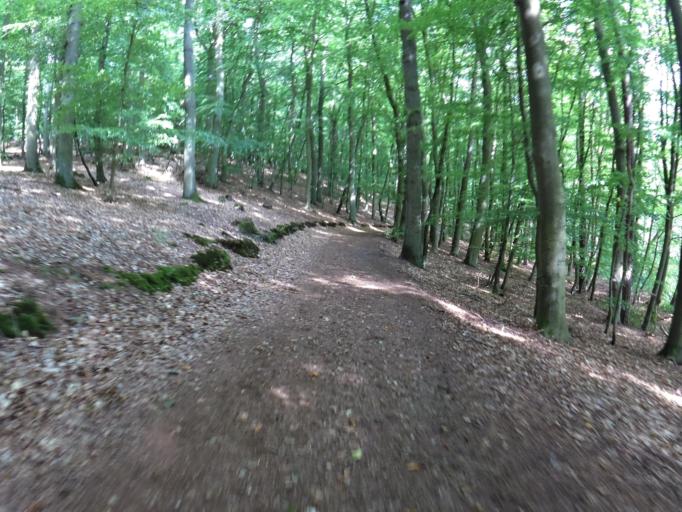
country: DE
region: Mecklenburg-Vorpommern
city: Seebad Bansin
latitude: 53.9522
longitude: 14.1079
